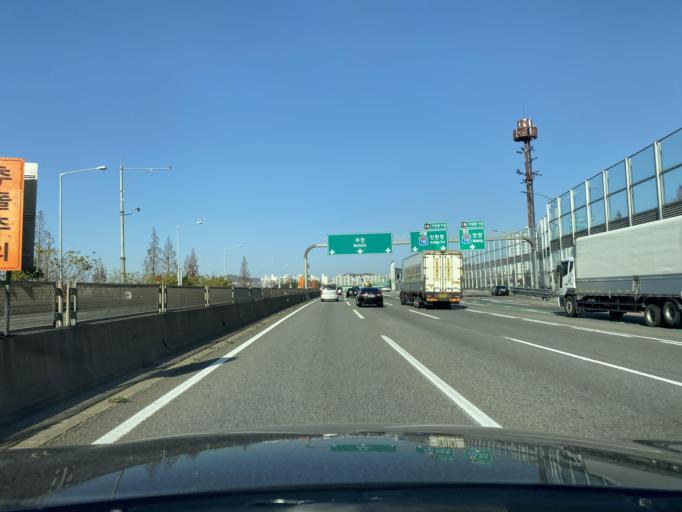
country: KR
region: Incheon
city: Incheon
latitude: 37.4258
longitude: 126.7374
